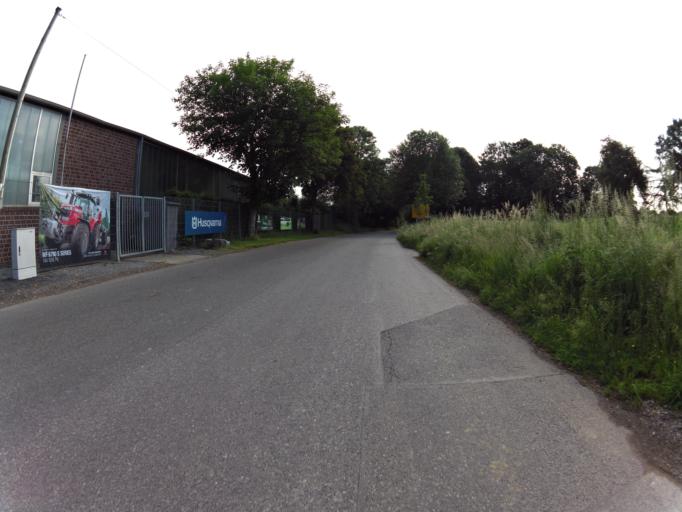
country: DE
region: North Rhine-Westphalia
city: Geilenkirchen
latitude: 50.9711
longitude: 6.1722
